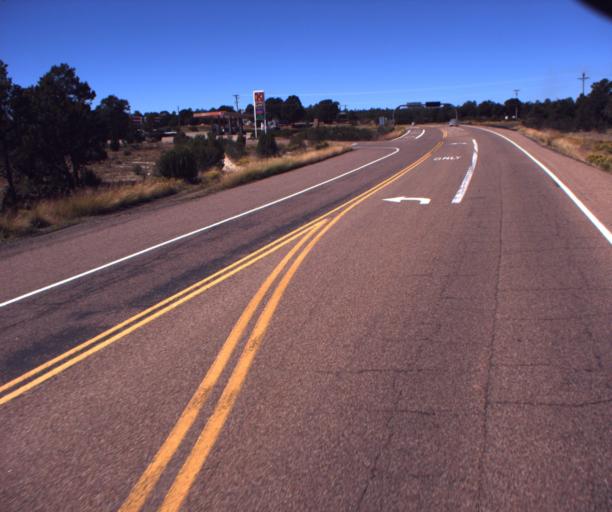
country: US
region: Arizona
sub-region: Navajo County
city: Heber-Overgaard
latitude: 34.4394
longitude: -110.6199
